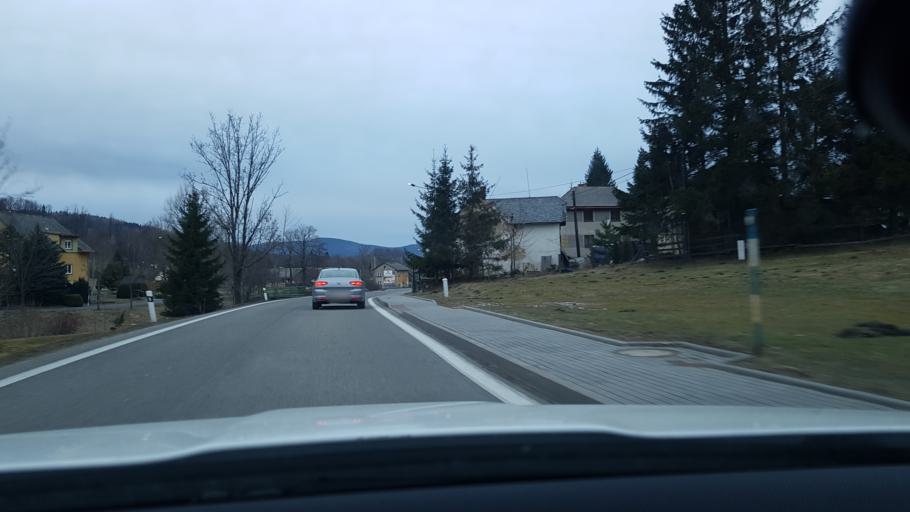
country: CZ
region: Olomoucky
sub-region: Okres Jesenik
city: Jesenik
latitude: 50.1676
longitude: 17.1956
